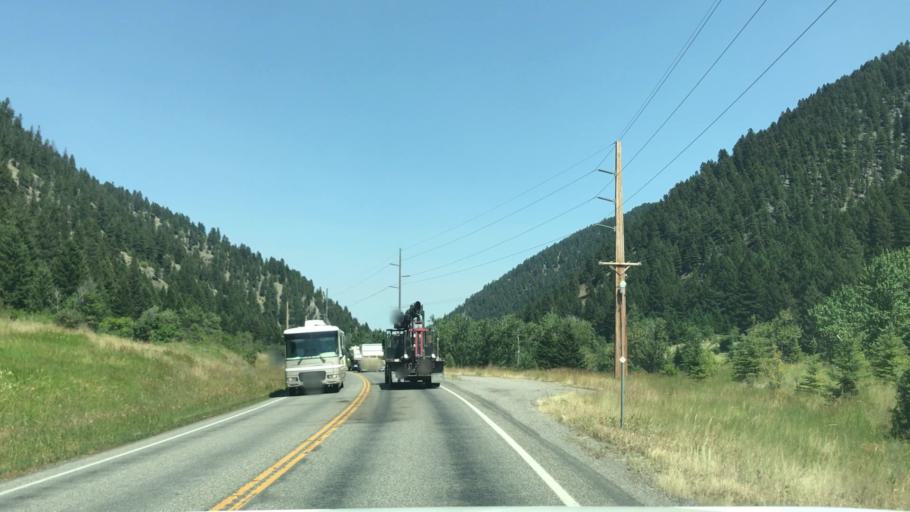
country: US
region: Montana
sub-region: Gallatin County
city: Four Corners
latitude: 45.5023
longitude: -111.2687
